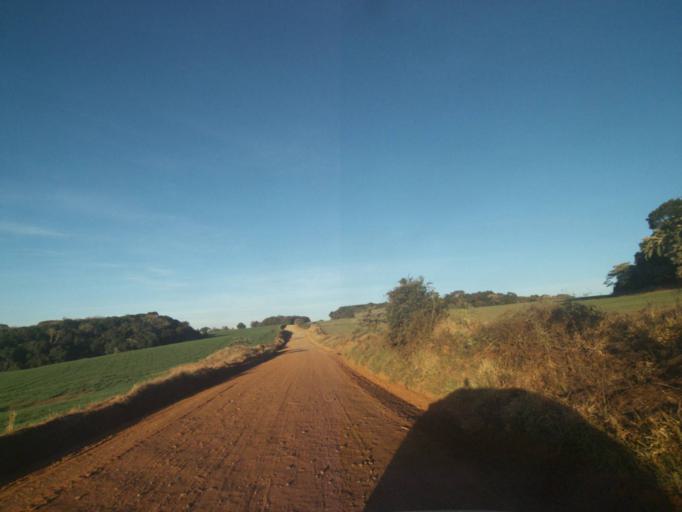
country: BR
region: Parana
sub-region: Tibagi
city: Tibagi
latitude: -24.5460
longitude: -50.5452
